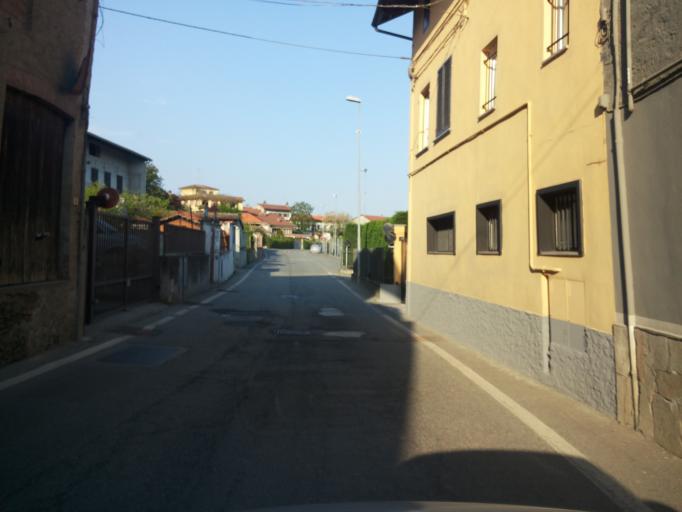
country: IT
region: Piedmont
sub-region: Provincia di Torino
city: Azeglio
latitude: 45.4239
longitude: 7.9958
